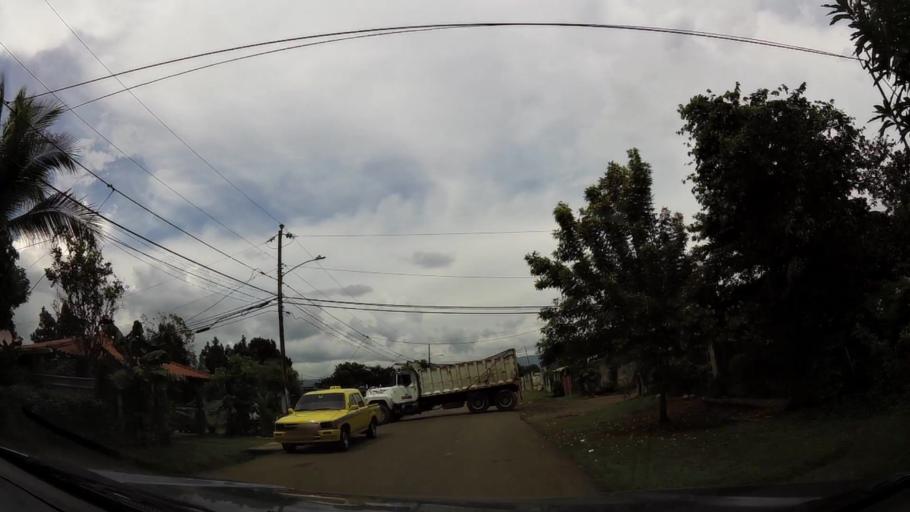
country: PA
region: Panama
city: Cabra Numero Uno
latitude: 9.1072
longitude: -79.3203
